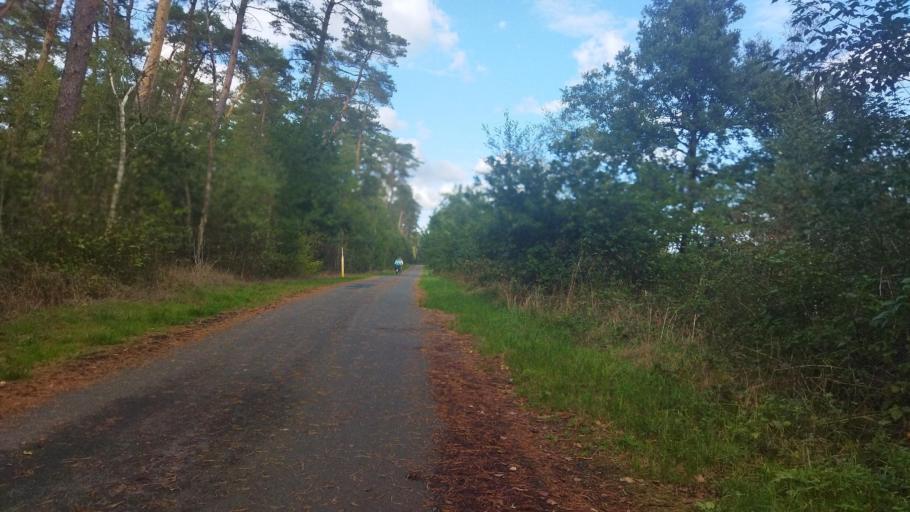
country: DE
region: North Rhine-Westphalia
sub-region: Regierungsbezirk Munster
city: Dulmen
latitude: 51.7916
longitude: 7.2566
